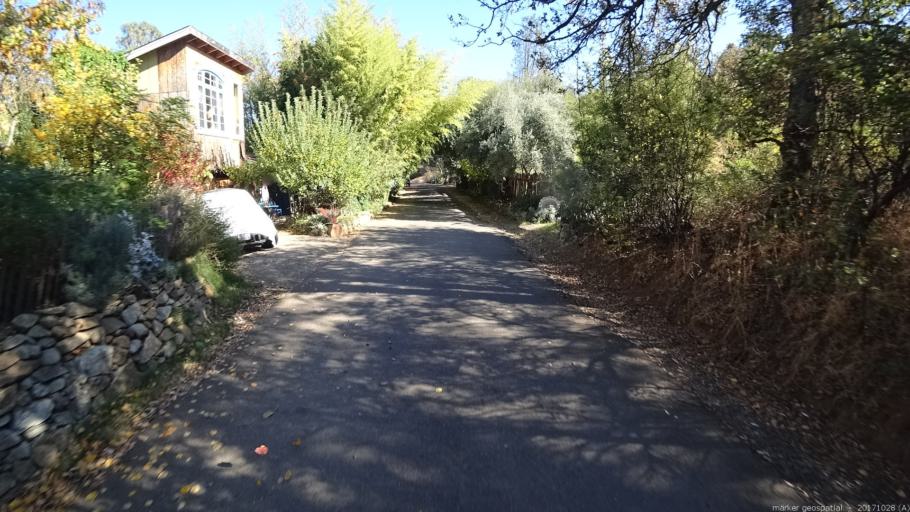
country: US
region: California
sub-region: Shasta County
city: Shasta
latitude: 40.5951
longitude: -122.4436
